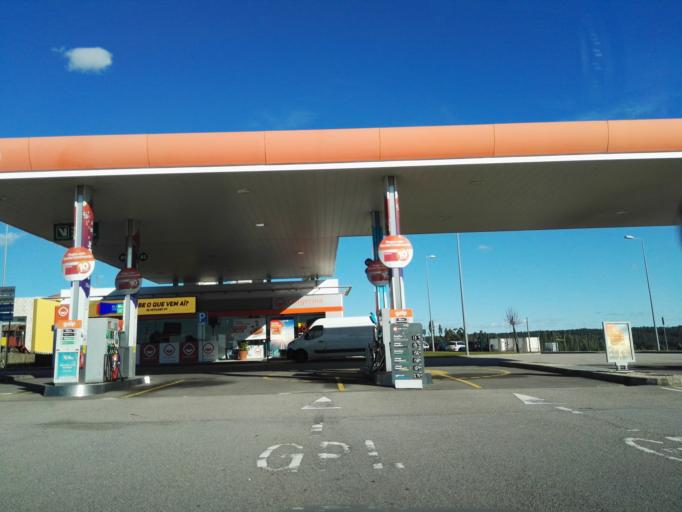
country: PT
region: Portalegre
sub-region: Nisa
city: Nisa
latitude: 39.5725
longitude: -7.7826
